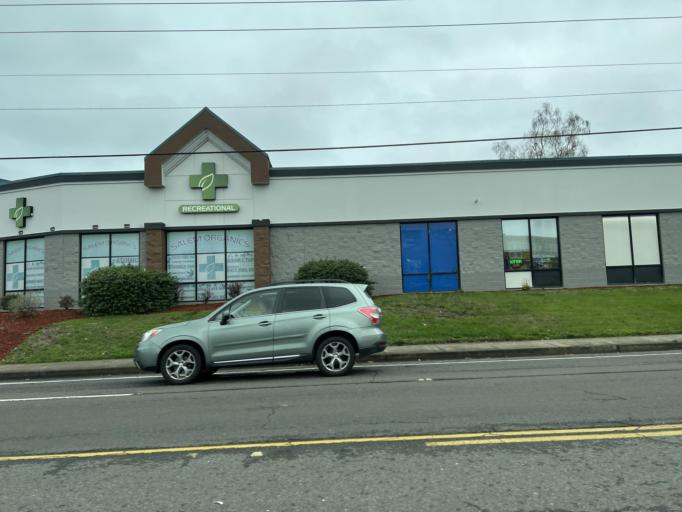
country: US
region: Oregon
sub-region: Marion County
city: Salem
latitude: 44.8839
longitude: -123.0315
